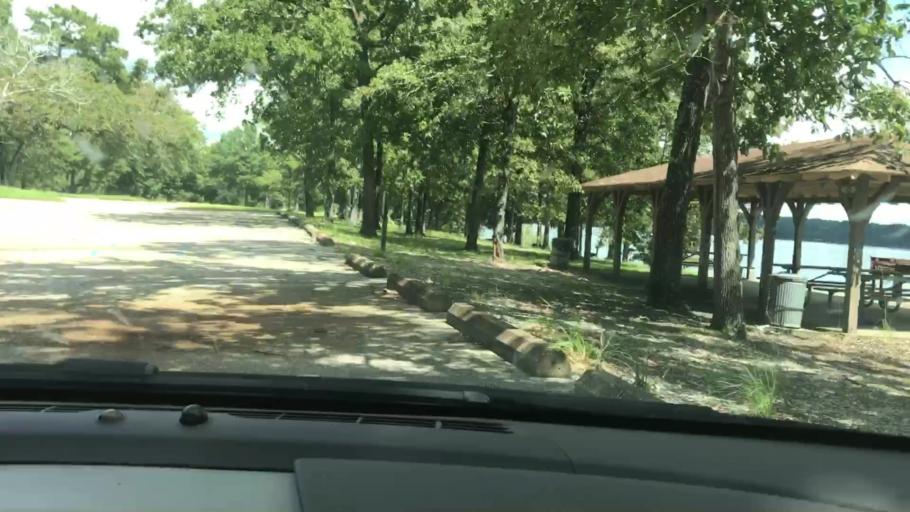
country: US
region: Georgia
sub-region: Clay County
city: Fort Gaines
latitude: 31.7339
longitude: -85.0807
